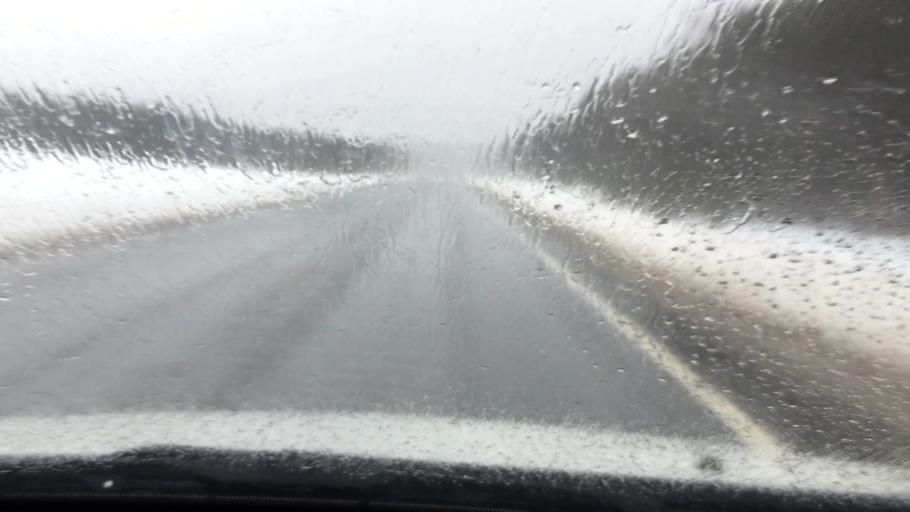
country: US
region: Michigan
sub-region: Antrim County
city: Mancelona
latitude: 44.9637
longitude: -85.0523
